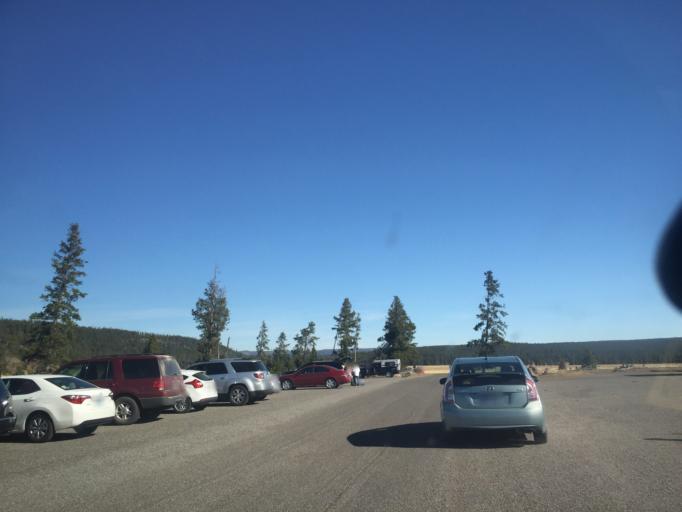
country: US
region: Montana
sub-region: Gallatin County
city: West Yellowstone
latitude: 44.5676
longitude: -110.8349
